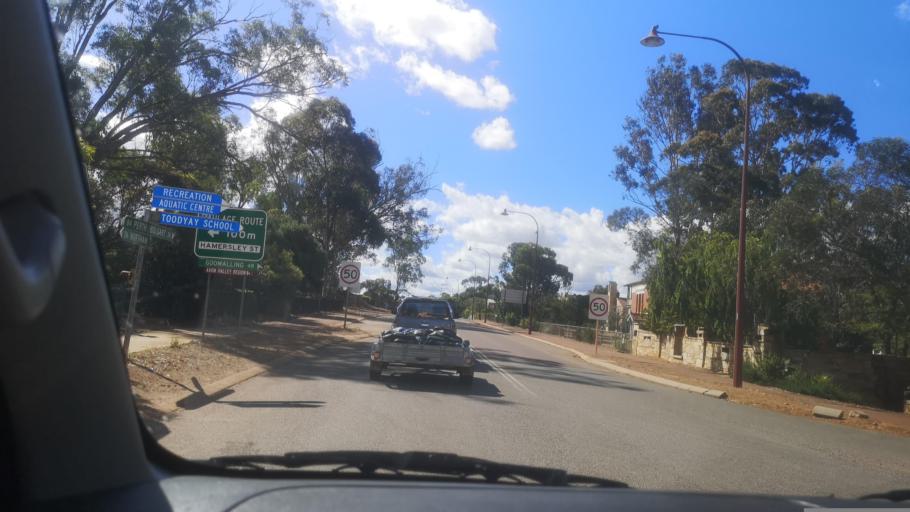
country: AU
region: Western Australia
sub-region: Toodyay
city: Toodyay
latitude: -31.5555
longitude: 116.4752
